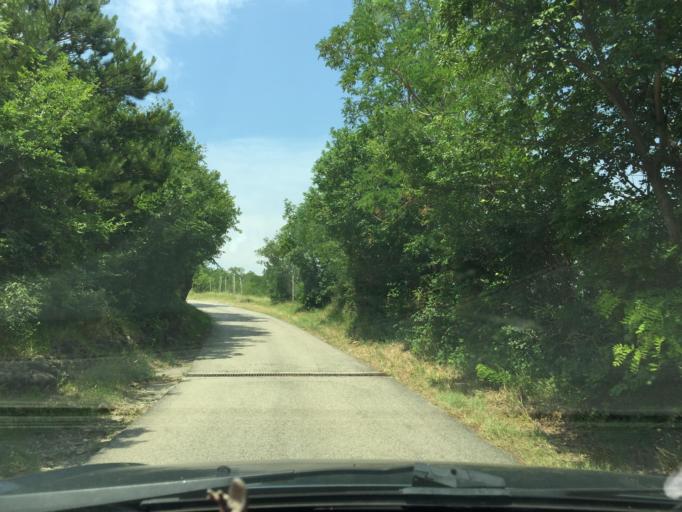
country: IT
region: Friuli Venezia Giulia
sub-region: Provincia di Trieste
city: Domio
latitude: 45.5938
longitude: 13.8302
